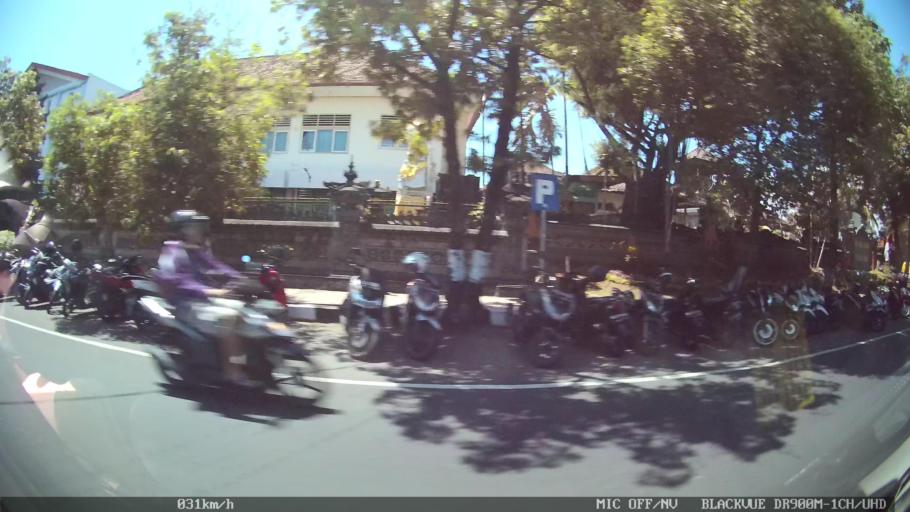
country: ID
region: Bali
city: Singaraja
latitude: -8.1119
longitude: 115.0909
